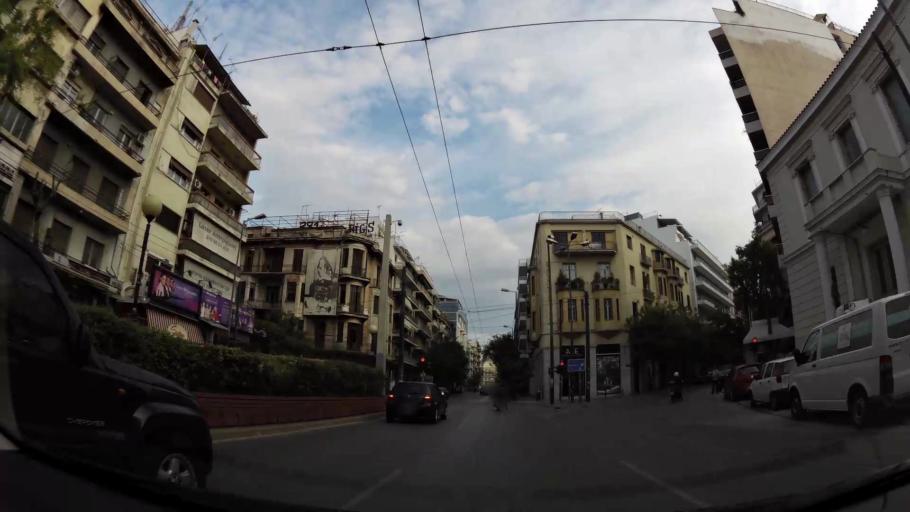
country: GR
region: Attica
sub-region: Nomarchia Athinas
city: Kipseli
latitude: 37.9997
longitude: 23.7333
